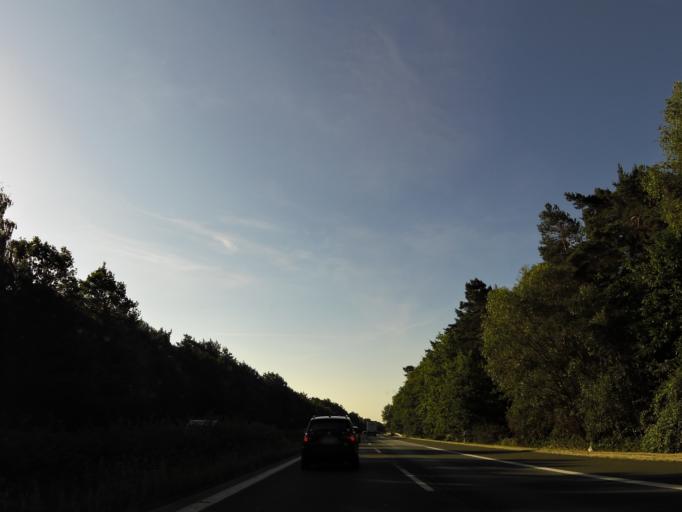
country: DE
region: Bavaria
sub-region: Regierungsbezirk Mittelfranken
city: Grossenseebach
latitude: 49.6628
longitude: 10.8891
